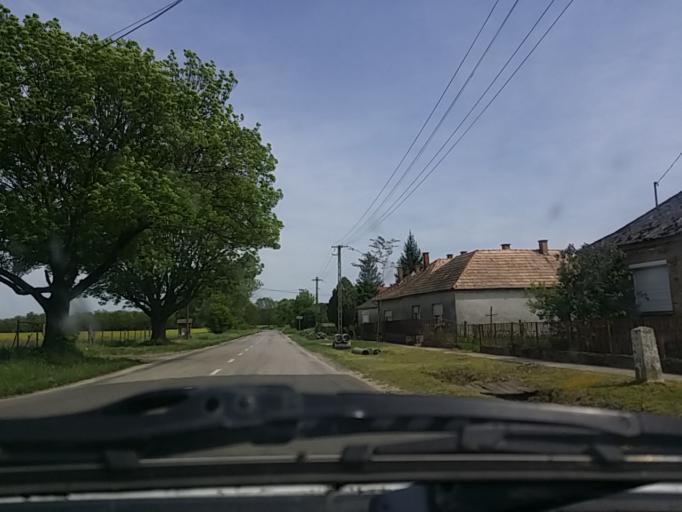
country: HU
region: Baranya
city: Vajszlo
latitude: 45.8547
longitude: 17.9970
